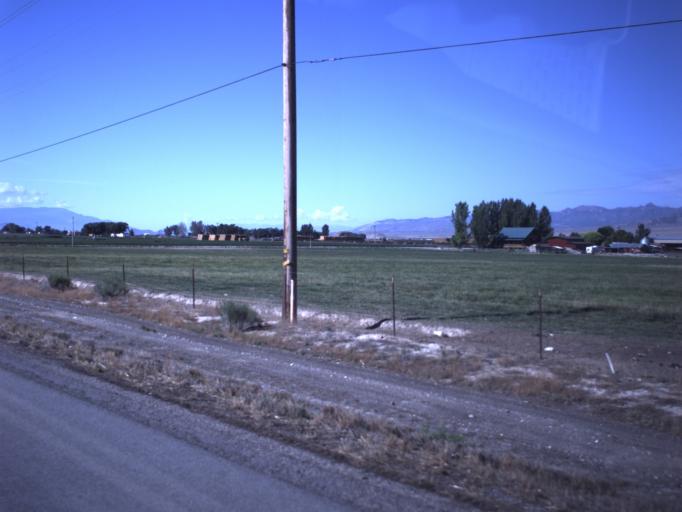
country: US
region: Utah
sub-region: Sanpete County
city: Centerfield
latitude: 39.0723
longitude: -111.8209
